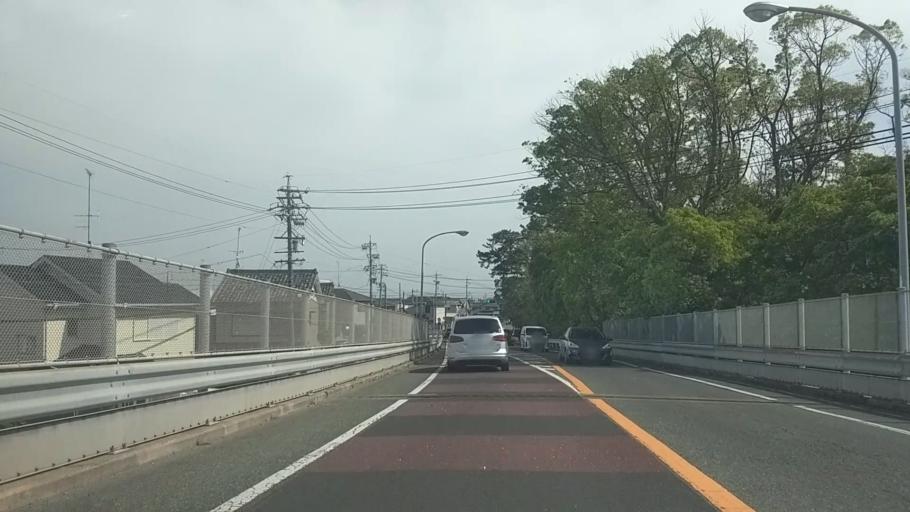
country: JP
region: Shizuoka
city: Kosai-shi
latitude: 34.6849
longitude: 137.6301
